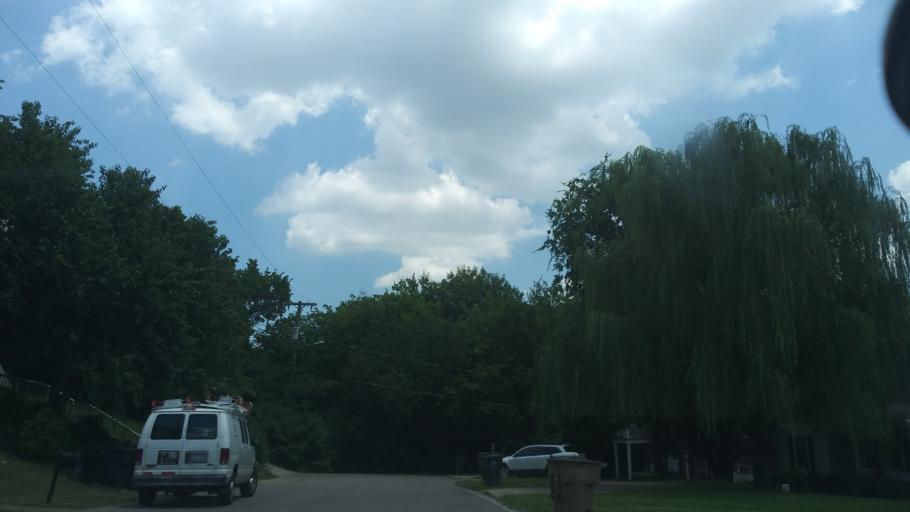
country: US
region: Tennessee
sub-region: Davidson County
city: Nashville
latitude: 36.1485
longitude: -86.8254
